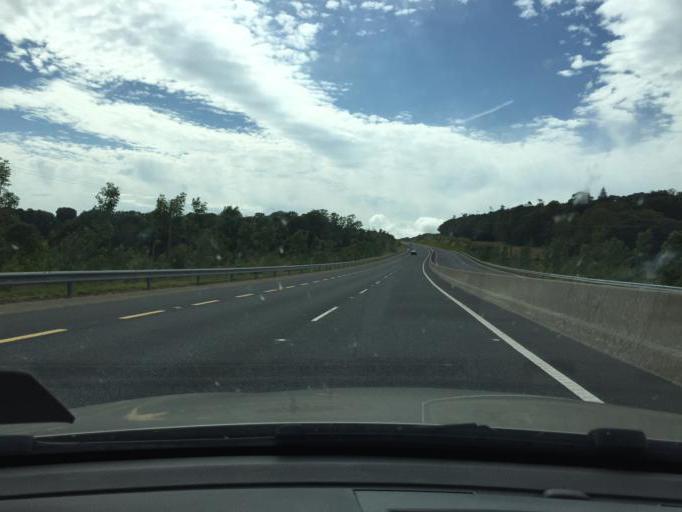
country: IE
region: Leinster
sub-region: Kilkenny
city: Mooncoin
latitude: 52.2358
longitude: -7.2116
